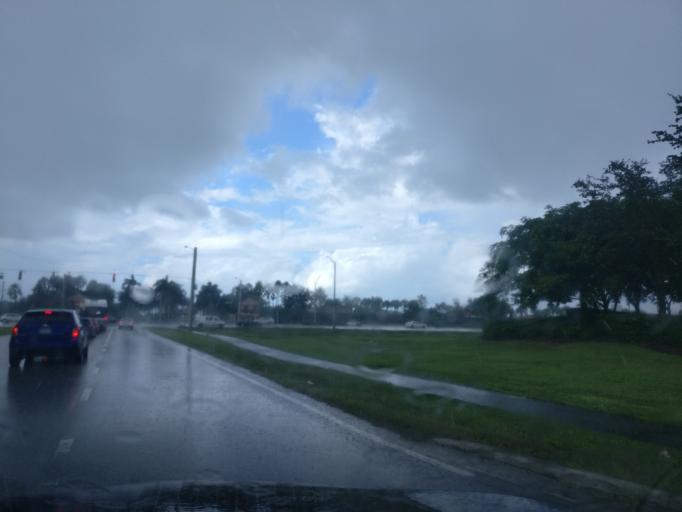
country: US
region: Florida
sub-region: Palm Beach County
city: Royal Palm Beach
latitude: 26.6880
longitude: -80.2007
